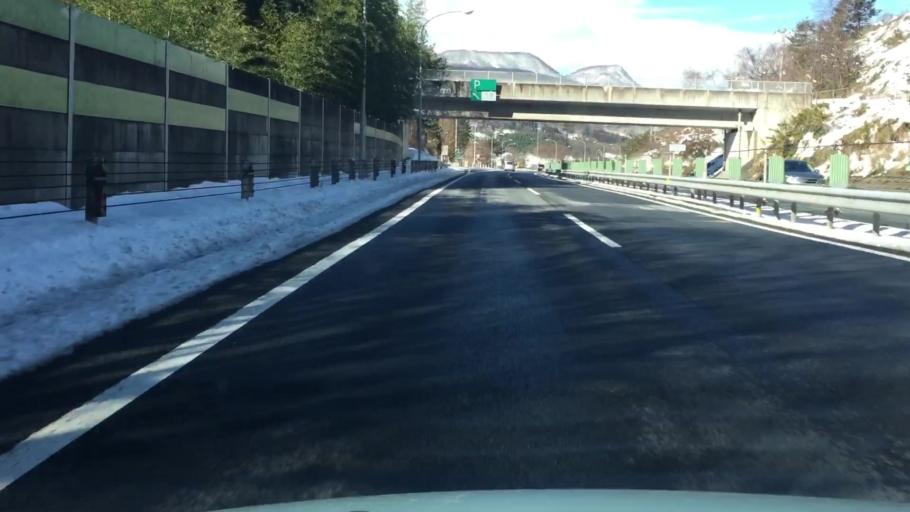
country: JP
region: Gunma
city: Numata
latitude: 36.6994
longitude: 138.9886
